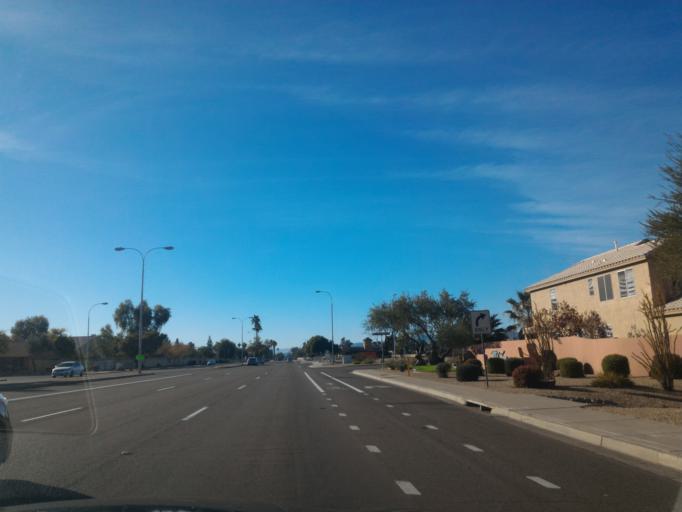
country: US
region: Arizona
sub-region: Maricopa County
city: Guadalupe
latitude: 33.3055
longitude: -111.9230
